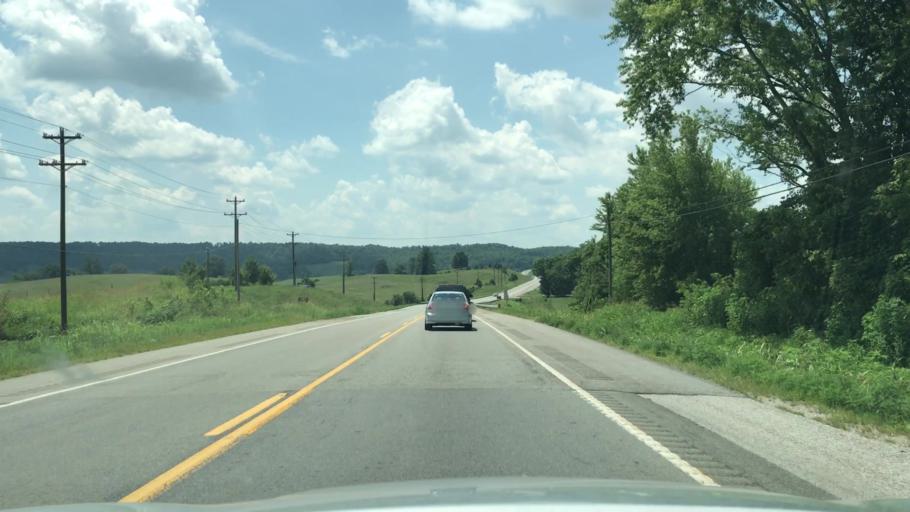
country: US
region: Tennessee
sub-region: Overton County
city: Livingston
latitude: 36.4204
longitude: -85.2838
